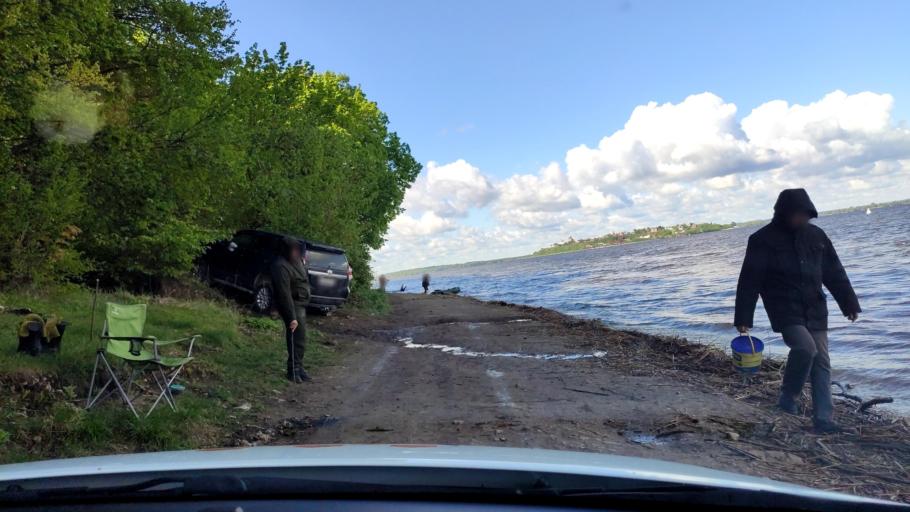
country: RU
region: Tatarstan
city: Sviyazhsk
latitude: 55.7808
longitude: 48.6974
